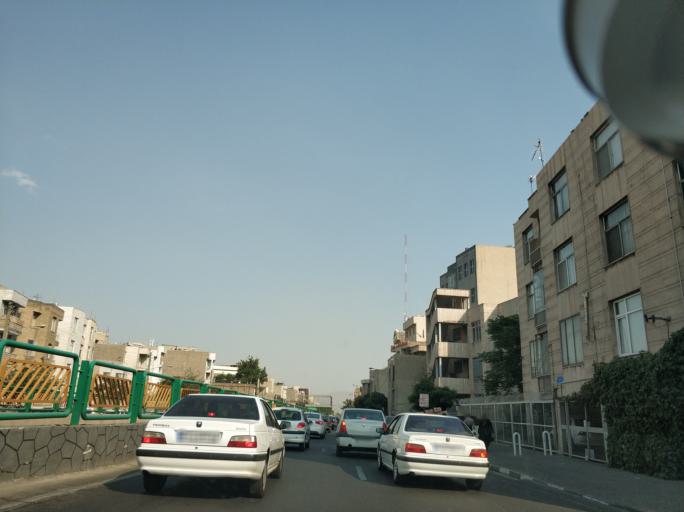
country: IR
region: Tehran
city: Tehran
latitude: 35.7343
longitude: 51.4600
